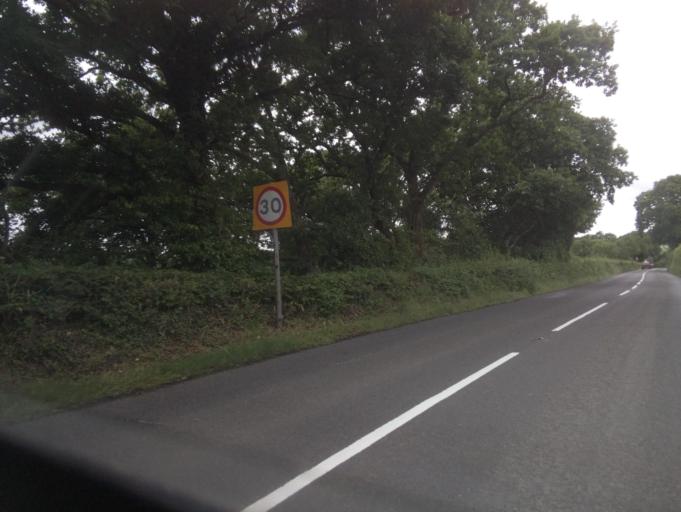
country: GB
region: England
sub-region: Devon
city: Exeter
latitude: 50.7080
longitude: -3.6026
